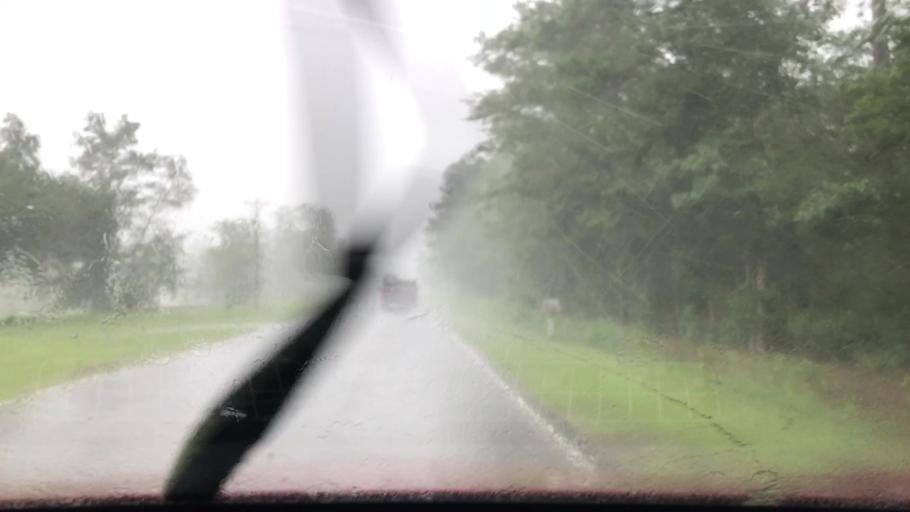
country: US
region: South Carolina
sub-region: Horry County
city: Red Hill
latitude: 33.9008
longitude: -78.9218
